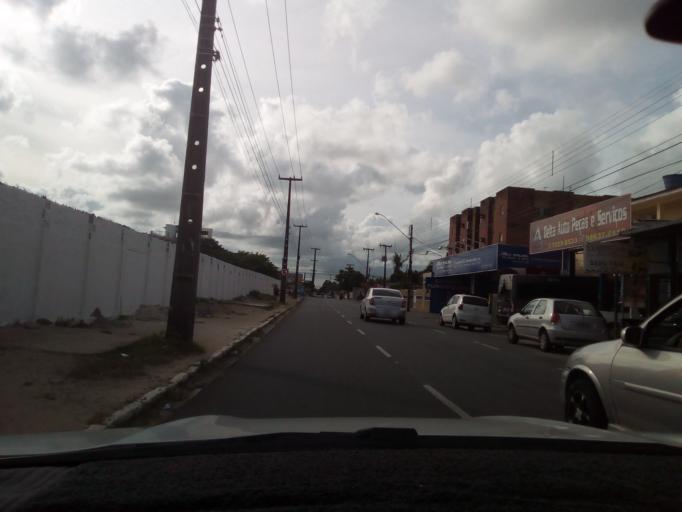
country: BR
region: Paraiba
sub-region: Joao Pessoa
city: Joao Pessoa
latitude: -7.1575
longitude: -34.8732
